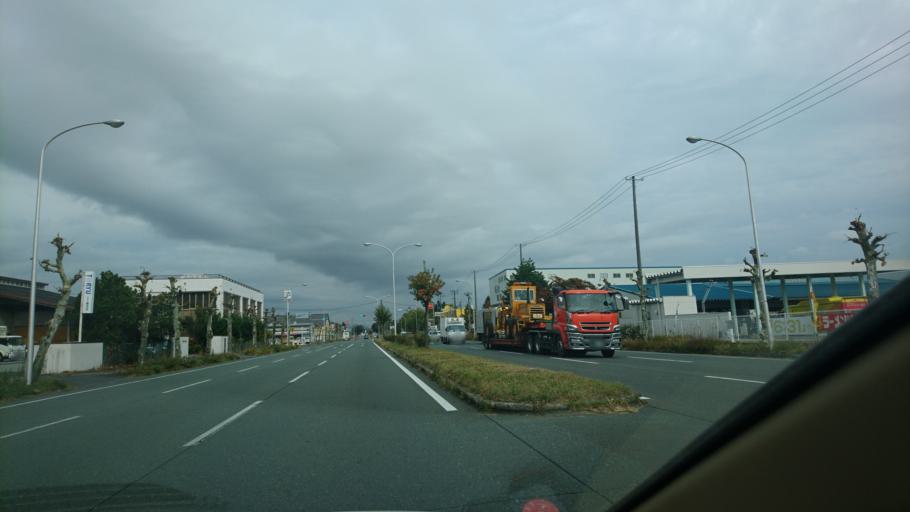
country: JP
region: Iwate
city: Morioka-shi
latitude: 39.6404
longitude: 141.1155
